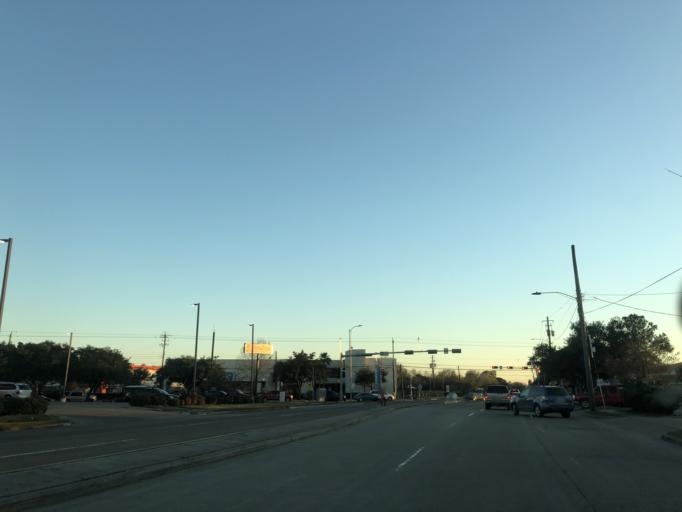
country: US
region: Texas
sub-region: Harris County
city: Bellaire
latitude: 29.6878
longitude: -95.5089
